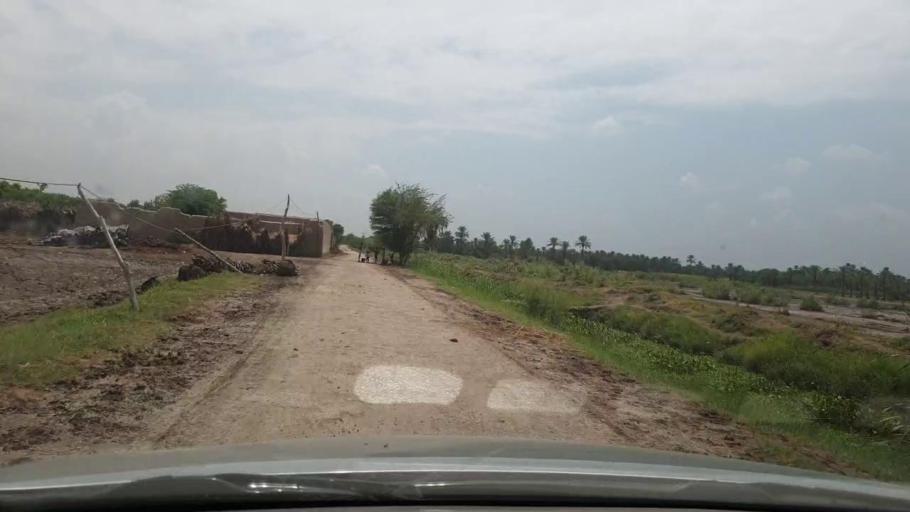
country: PK
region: Sindh
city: Kot Diji
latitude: 27.4217
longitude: 68.7600
